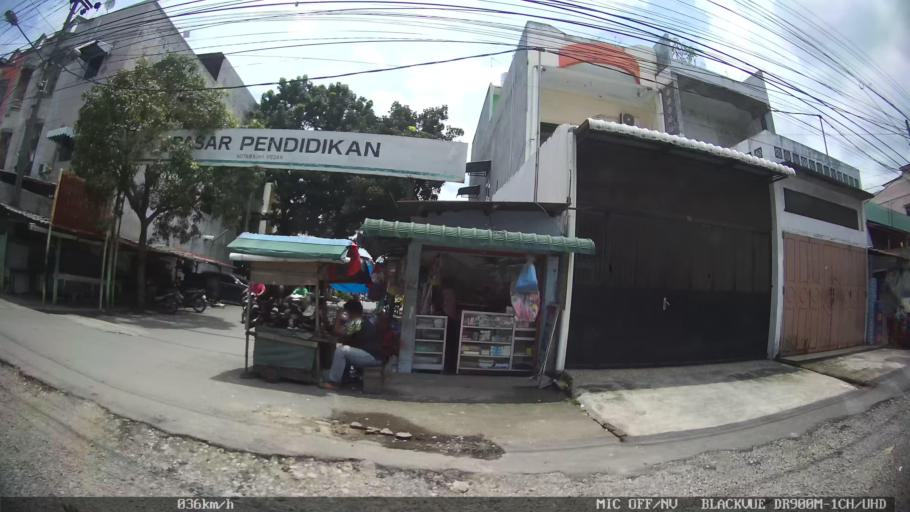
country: ID
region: North Sumatra
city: Medan
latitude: 3.6168
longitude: 98.6823
